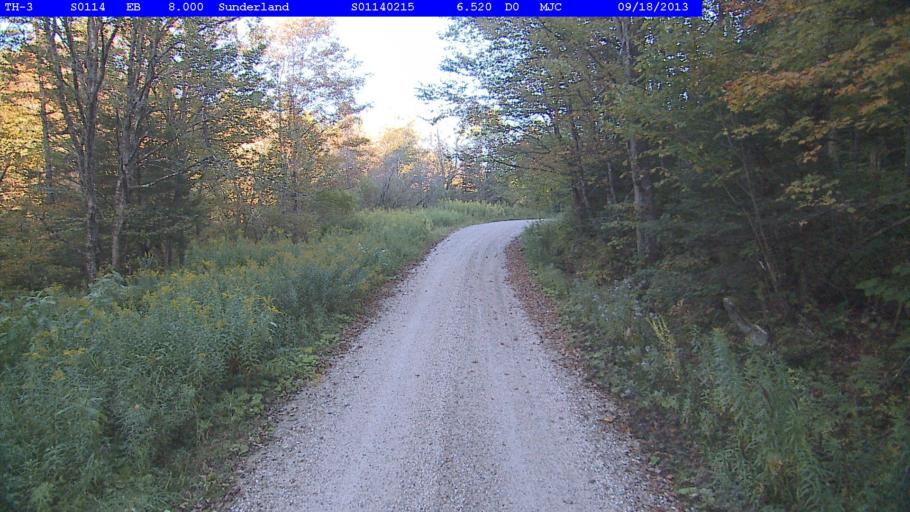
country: US
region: Vermont
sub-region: Bennington County
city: Arlington
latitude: 43.0541
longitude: -73.0580
